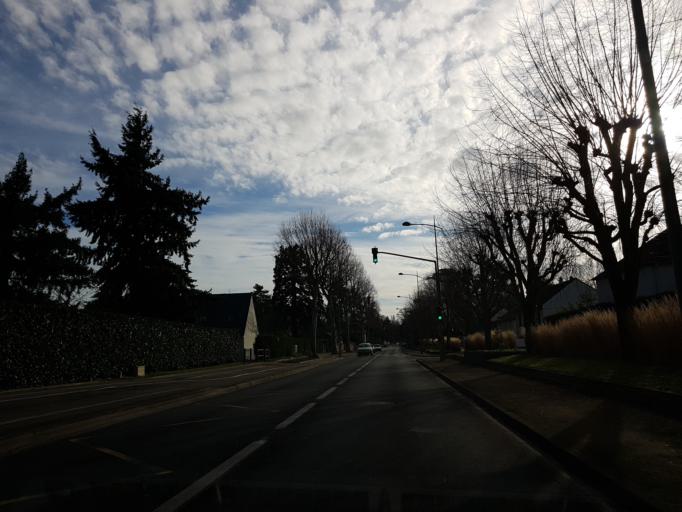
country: FR
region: Centre
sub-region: Departement du Loiret
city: Saint-Jean-le-Blanc
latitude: 47.8855
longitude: 1.9287
